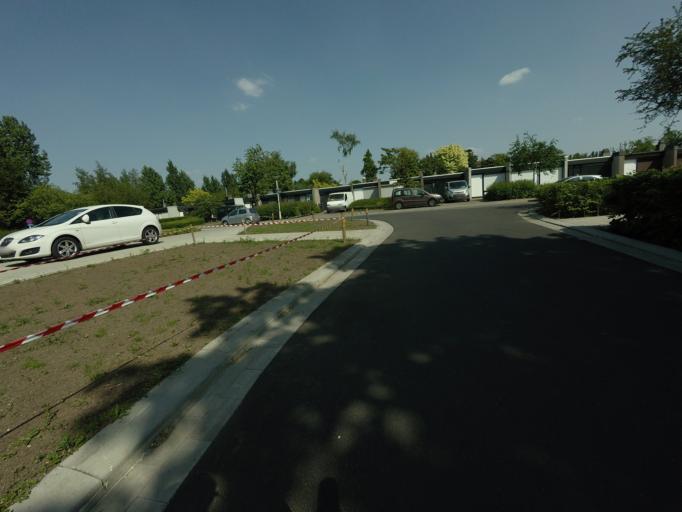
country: BE
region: Flanders
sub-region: Provincie Antwerpen
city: Borsbeek
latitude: 51.1920
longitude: 4.4723
